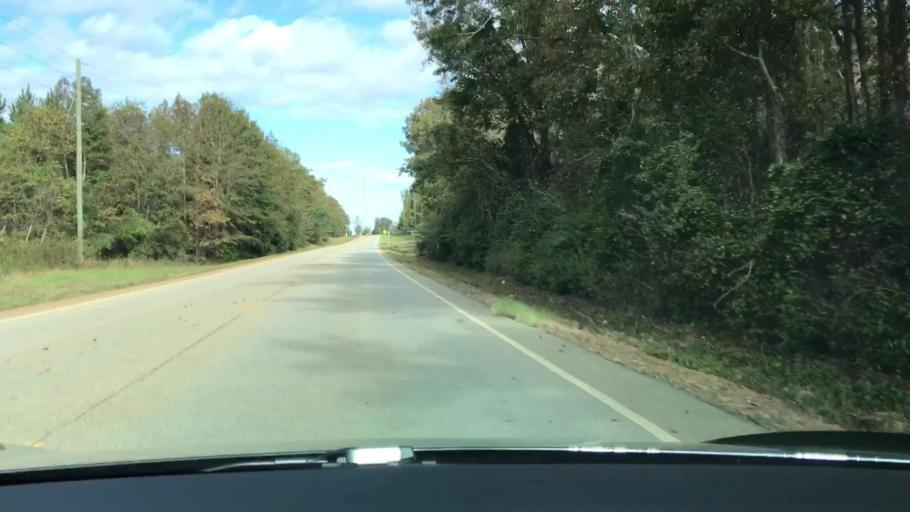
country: US
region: Georgia
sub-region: Jefferson County
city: Louisville
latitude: 33.0937
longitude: -82.4178
